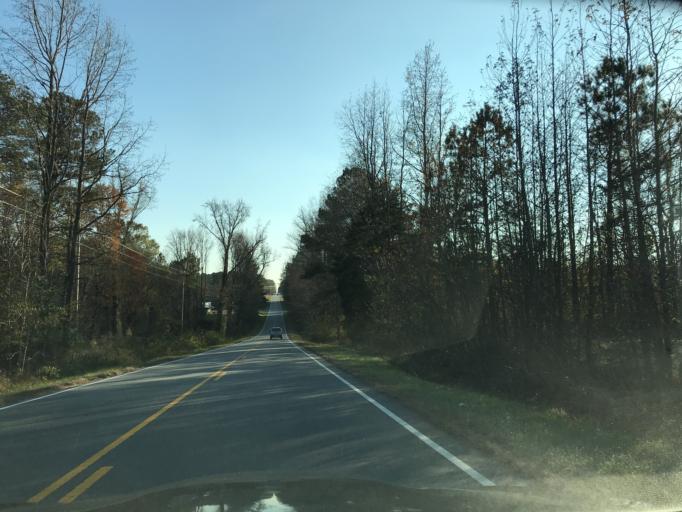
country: US
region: North Carolina
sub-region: Granville County
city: Creedmoor
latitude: 36.1072
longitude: -78.6884
